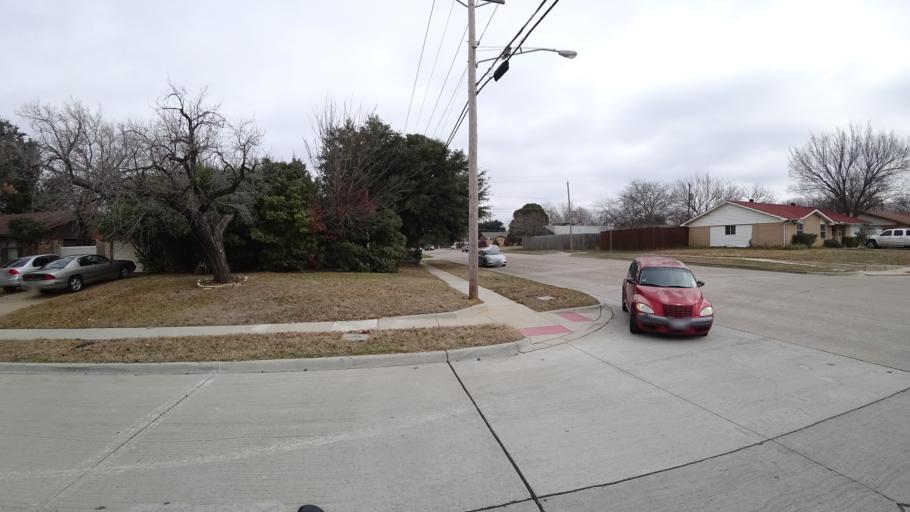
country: US
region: Texas
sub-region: Denton County
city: Lewisville
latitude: 33.0351
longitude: -97.0205
